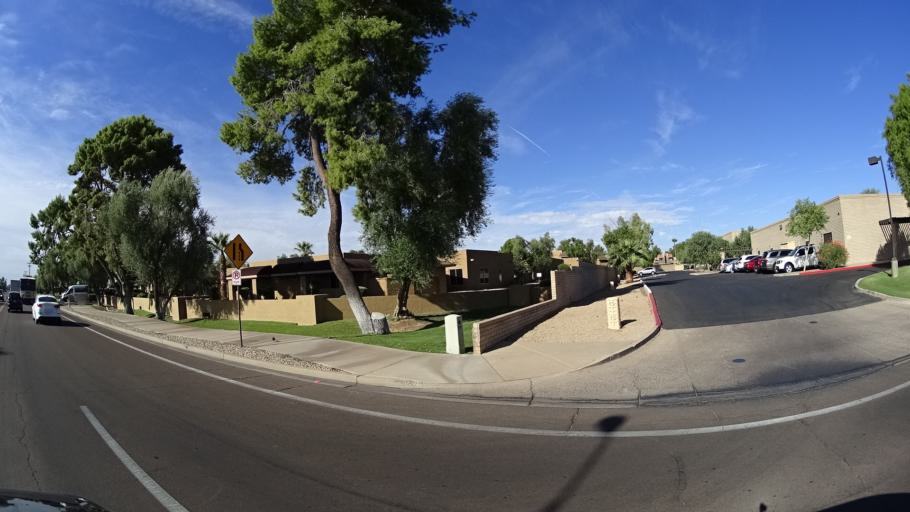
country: US
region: Arizona
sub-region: Maricopa County
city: Scottsdale
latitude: 33.4782
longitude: -111.9349
